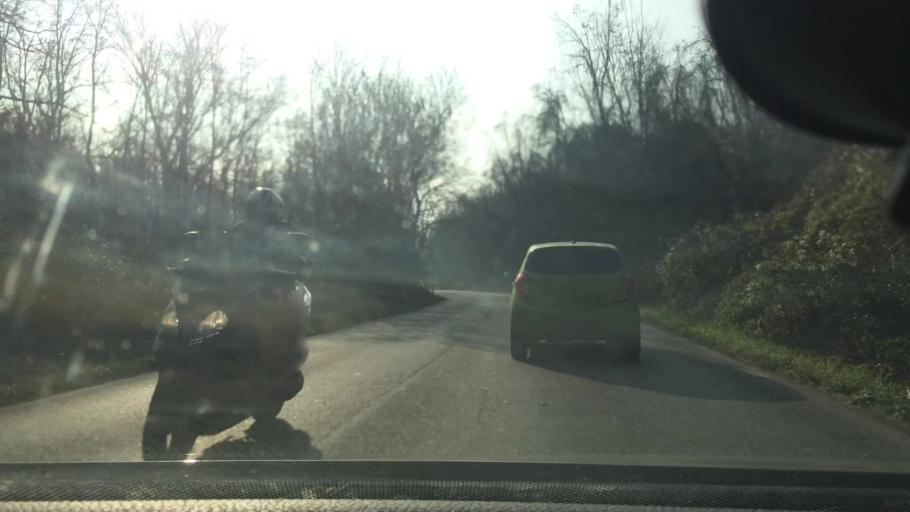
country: IT
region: Lombardy
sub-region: Citta metropolitana di Milano
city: Cesate
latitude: 45.5922
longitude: 9.0935
